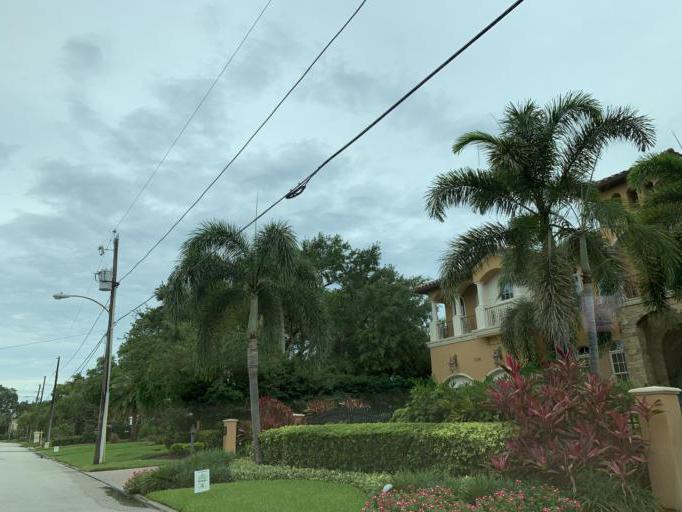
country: US
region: Florida
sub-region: Pinellas County
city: Saint Petersburg
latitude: 27.7943
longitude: -82.6194
